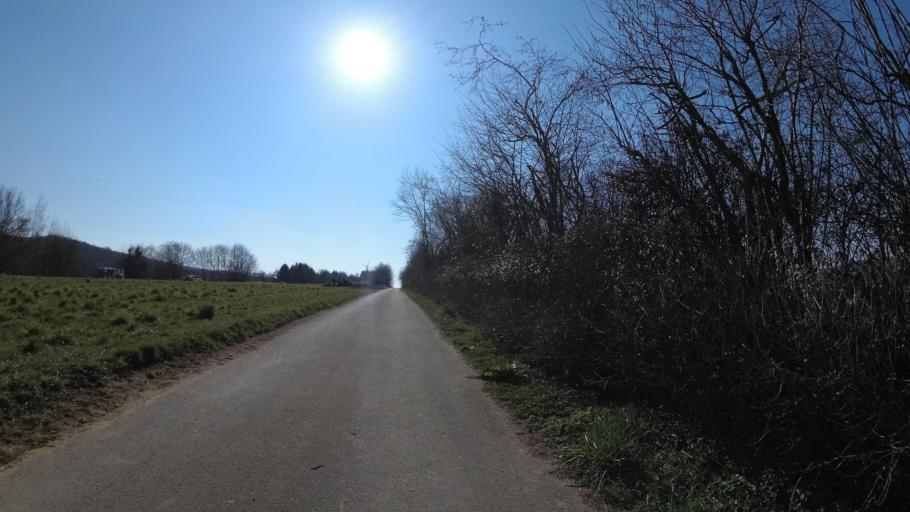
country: DE
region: Rheinland-Pfalz
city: Pfeffelbach
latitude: 49.5352
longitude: 7.3200
